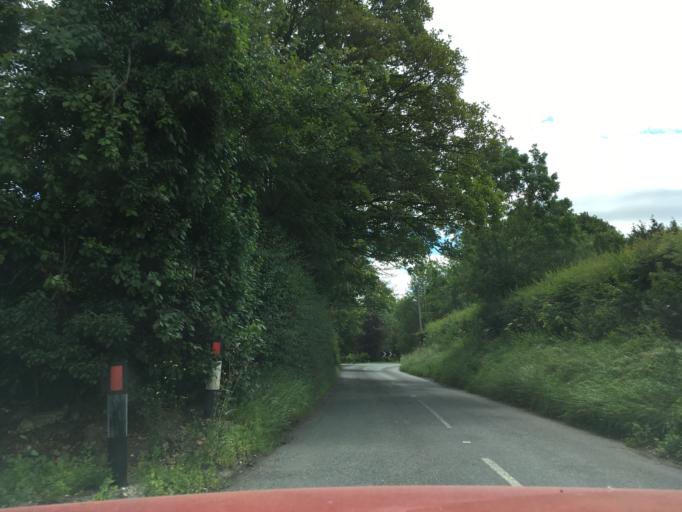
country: GB
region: England
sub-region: West Berkshire
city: Wickham
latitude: 51.4696
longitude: -1.4428
